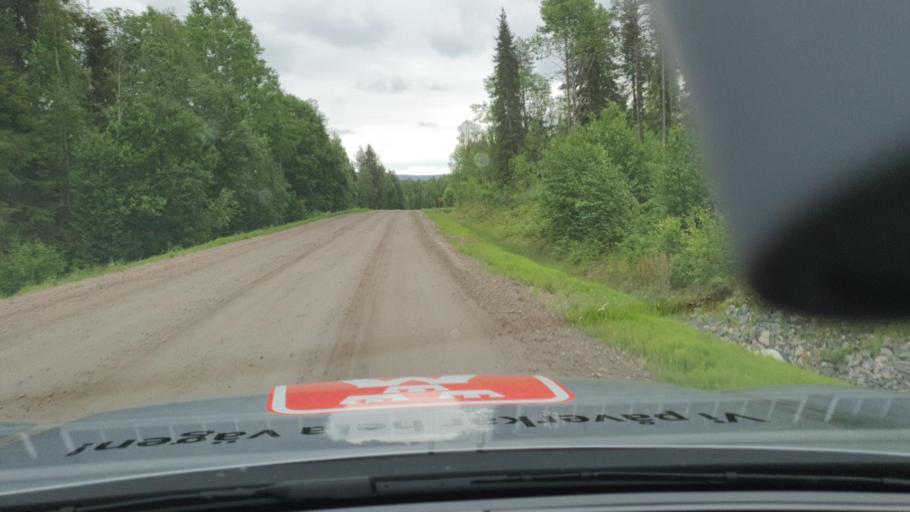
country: SE
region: Norrbotten
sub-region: Overtornea Kommun
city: OEvertornea
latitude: 66.4174
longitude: 23.5822
